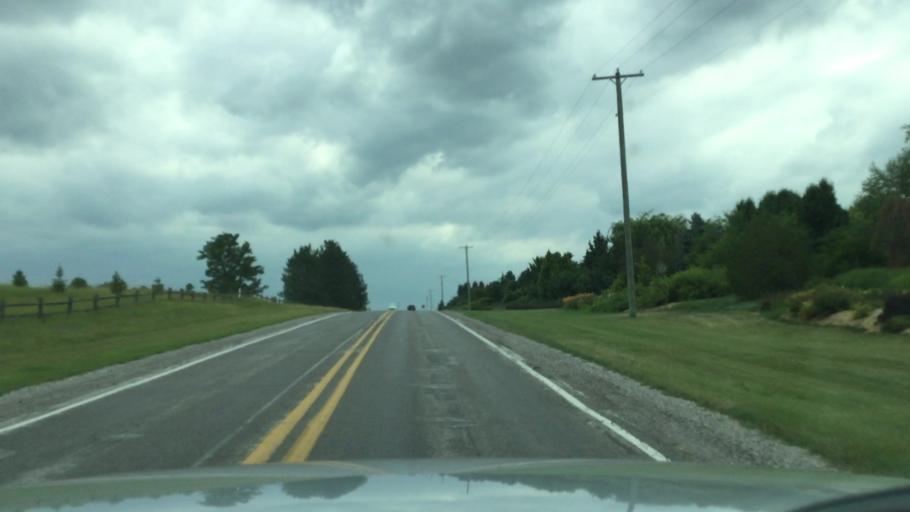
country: US
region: Michigan
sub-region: Saginaw County
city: Frankenmuth
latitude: 43.3263
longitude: -83.7581
